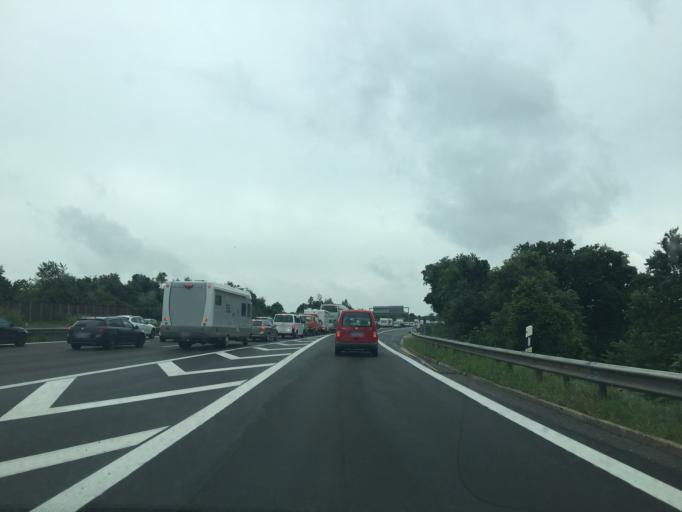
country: DE
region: Bavaria
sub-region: Upper Bavaria
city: Holzkirchen
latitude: 47.8970
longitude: 11.7234
